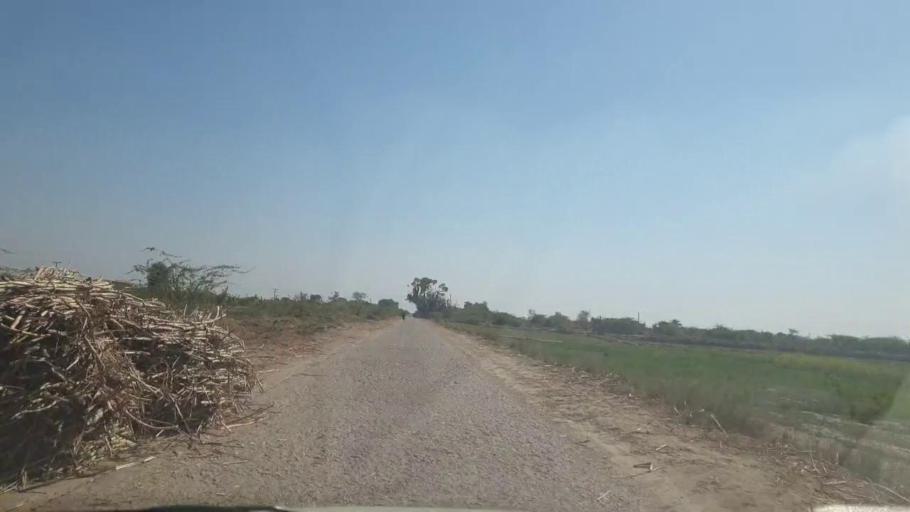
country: PK
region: Sindh
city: Mirpur Khas
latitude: 25.4845
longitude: 69.1703
